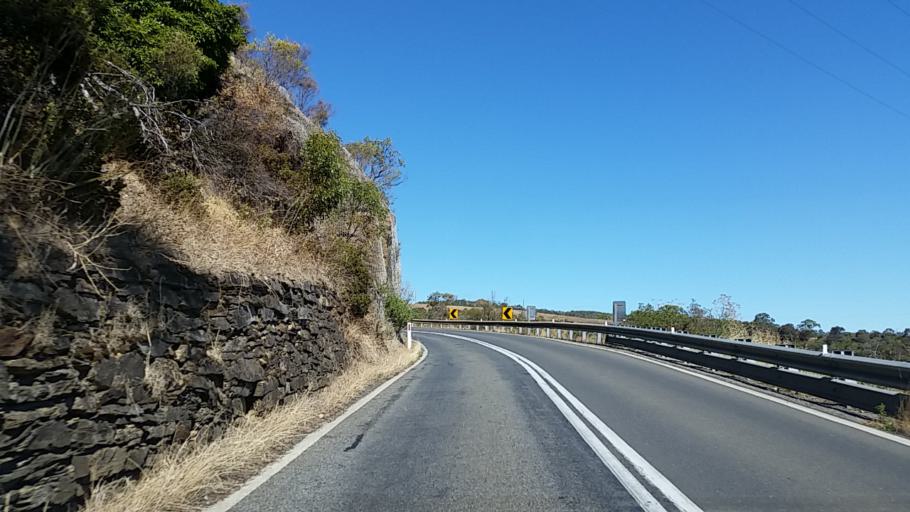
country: AU
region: South Australia
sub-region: Burnside
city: Beaumont
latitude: -34.9504
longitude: 138.6810
